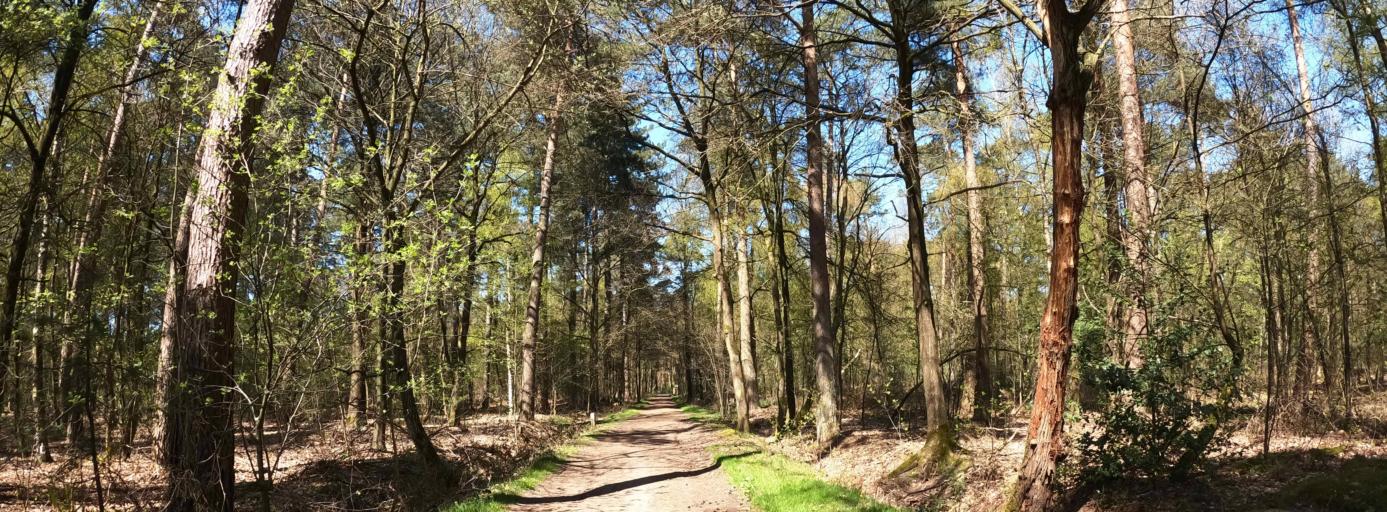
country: BE
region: Flanders
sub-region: Provincie Antwerpen
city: Kalmthout
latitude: 51.3660
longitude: 4.4848
